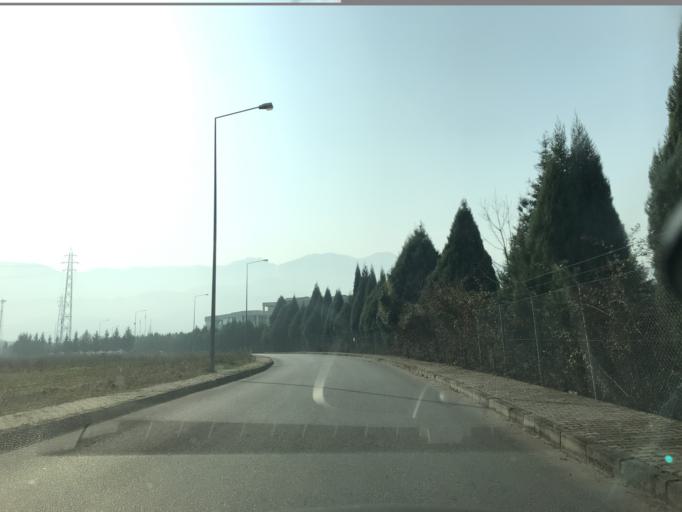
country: TR
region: Duzce
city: Duzce
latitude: 40.7866
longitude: 31.1533
